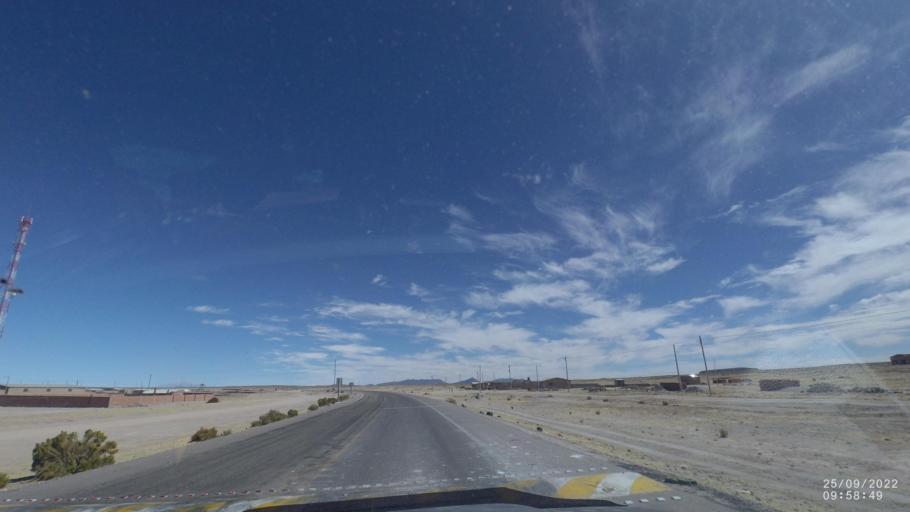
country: BO
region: Potosi
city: Colchani
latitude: -20.2994
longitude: -66.9332
